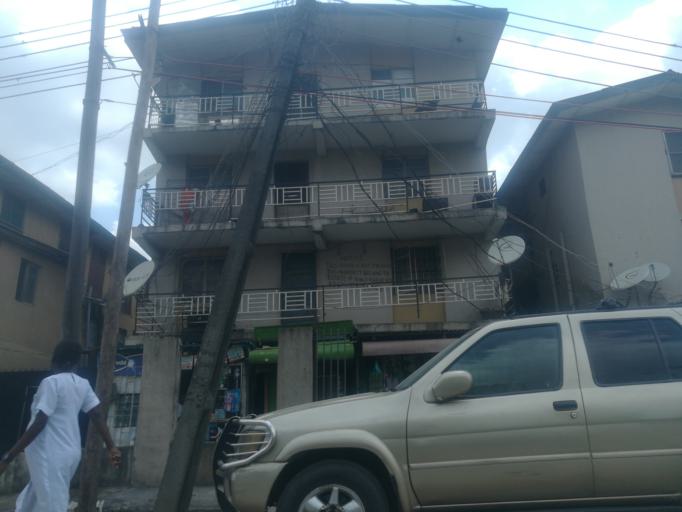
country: NG
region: Lagos
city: Somolu
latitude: 6.5561
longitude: 3.3872
